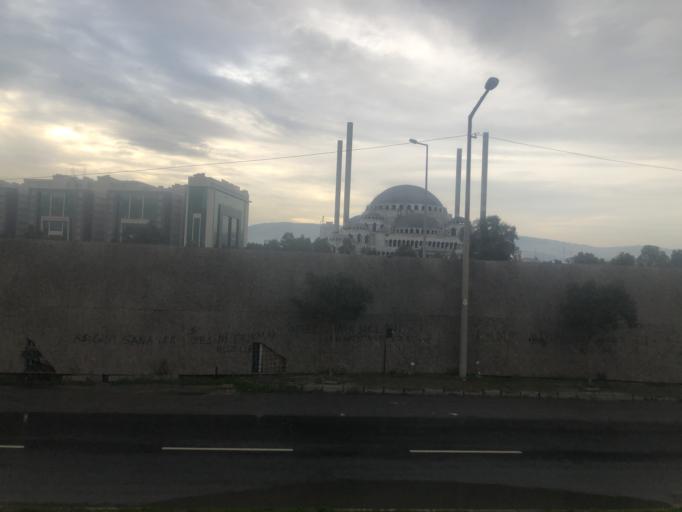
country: TR
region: Izmir
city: Buca
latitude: 38.4456
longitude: 27.1752
